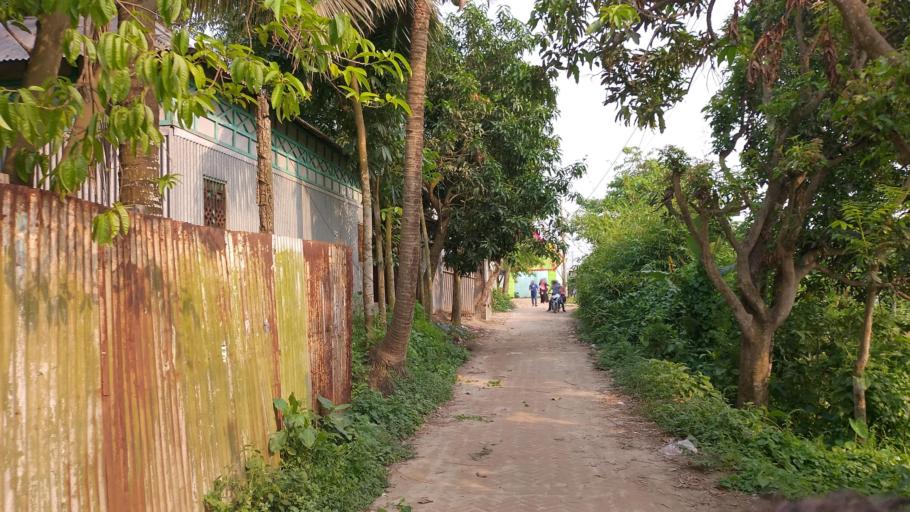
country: BD
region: Dhaka
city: Azimpur
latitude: 23.6676
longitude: 90.3157
